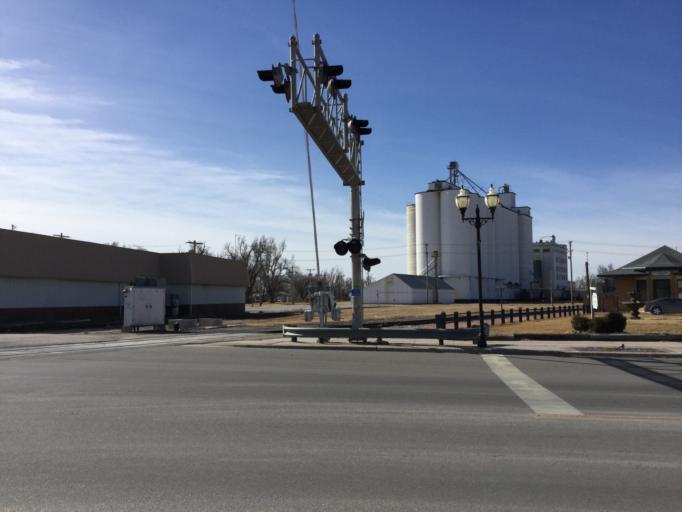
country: US
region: Kansas
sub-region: Rice County
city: Sterling
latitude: 38.2074
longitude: -98.2070
